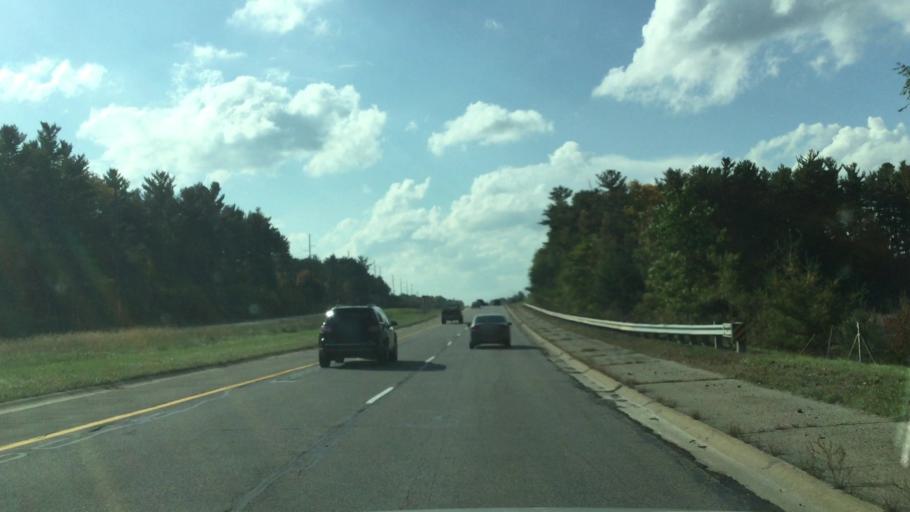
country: US
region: Michigan
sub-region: Oakland County
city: Milford
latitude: 42.6423
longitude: -83.6069
